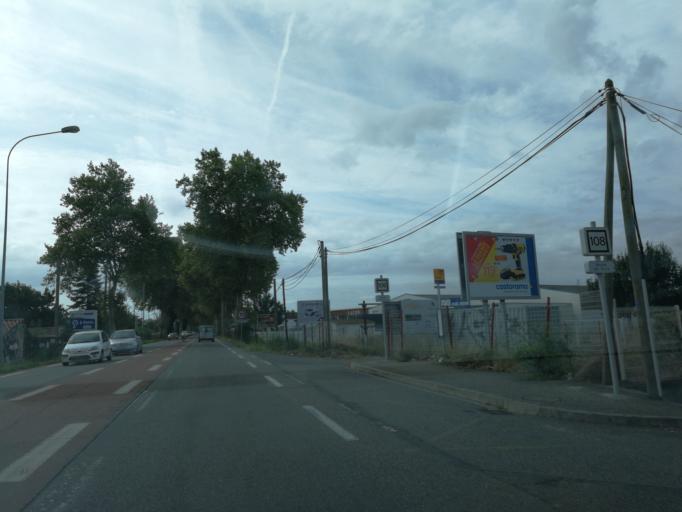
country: FR
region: Midi-Pyrenees
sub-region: Departement de la Haute-Garonne
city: Saint-Alban
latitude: 43.6836
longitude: 1.4064
